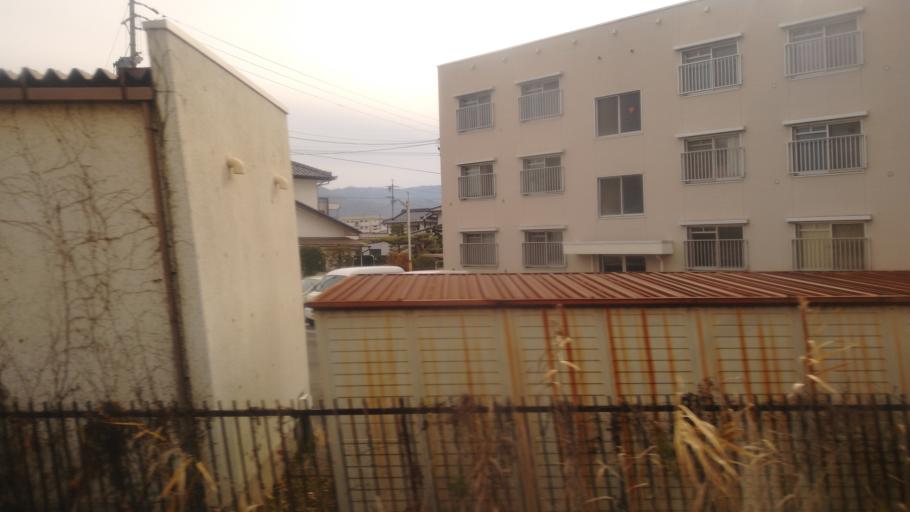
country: JP
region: Nagano
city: Nagano-shi
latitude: 36.5706
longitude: 138.1330
